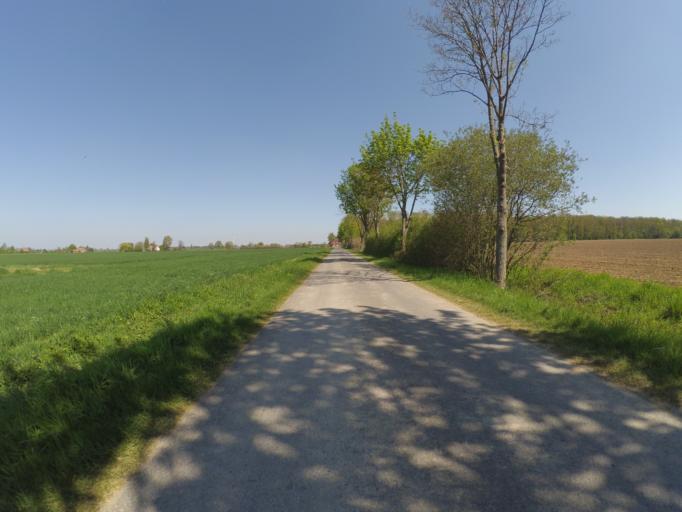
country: DE
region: North Rhine-Westphalia
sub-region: Regierungsbezirk Munster
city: Nordkirchen
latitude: 51.7712
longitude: 7.5549
